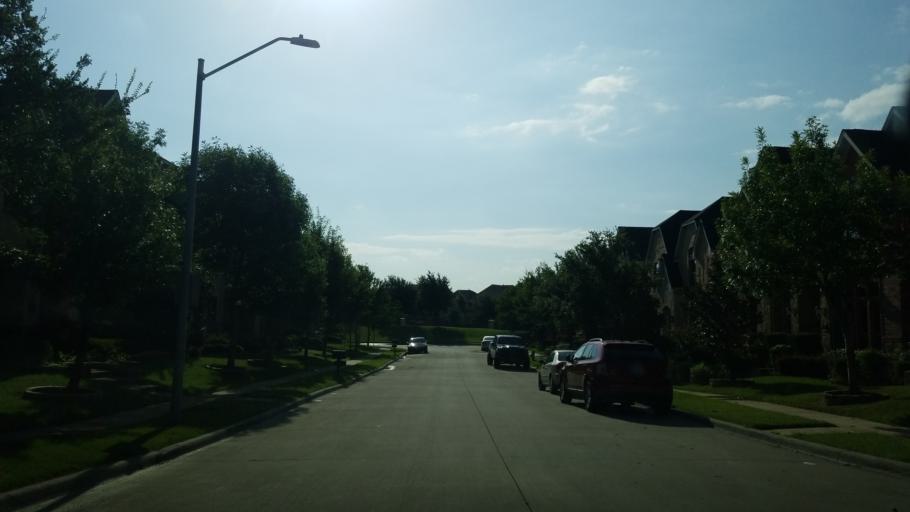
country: US
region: Texas
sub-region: Dallas County
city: Coppell
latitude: 32.9233
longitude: -96.9750
